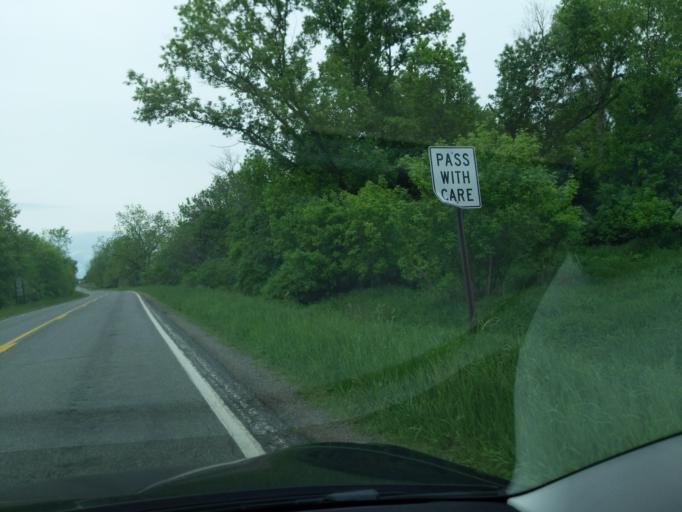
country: US
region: Michigan
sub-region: Ingham County
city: Mason
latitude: 42.5347
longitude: -84.4232
